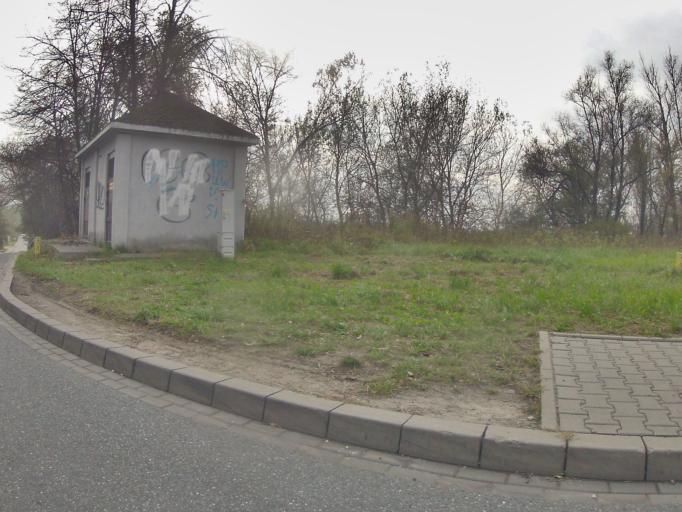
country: PL
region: Lesser Poland Voivodeship
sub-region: Powiat wielicki
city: Kokotow
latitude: 50.0642
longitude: 20.0817
